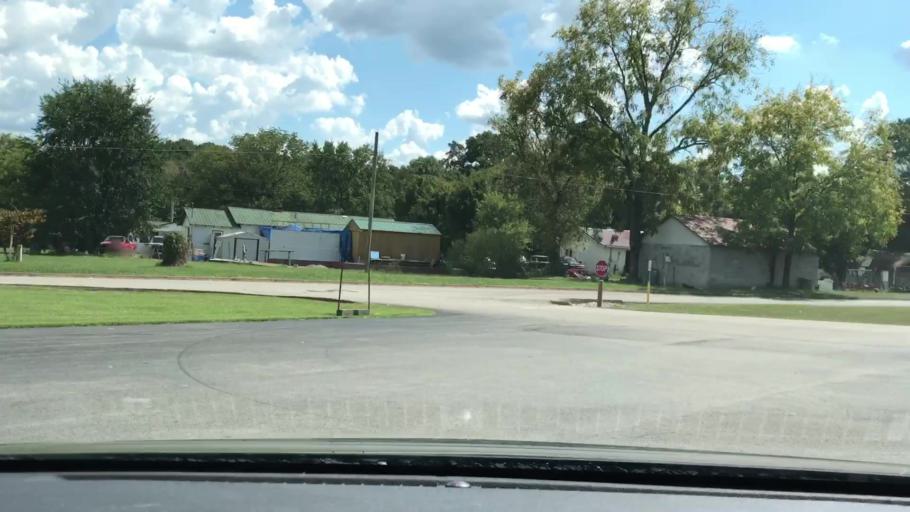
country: US
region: Kentucky
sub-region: Metcalfe County
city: Edmonton
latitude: 36.9882
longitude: -85.6381
